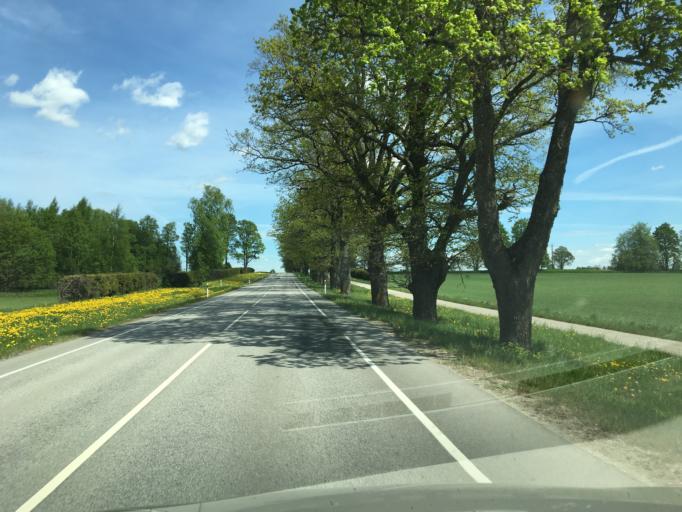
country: EE
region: Vorumaa
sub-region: Antsla vald
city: Vana-Antsla
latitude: 57.9135
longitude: 26.3025
